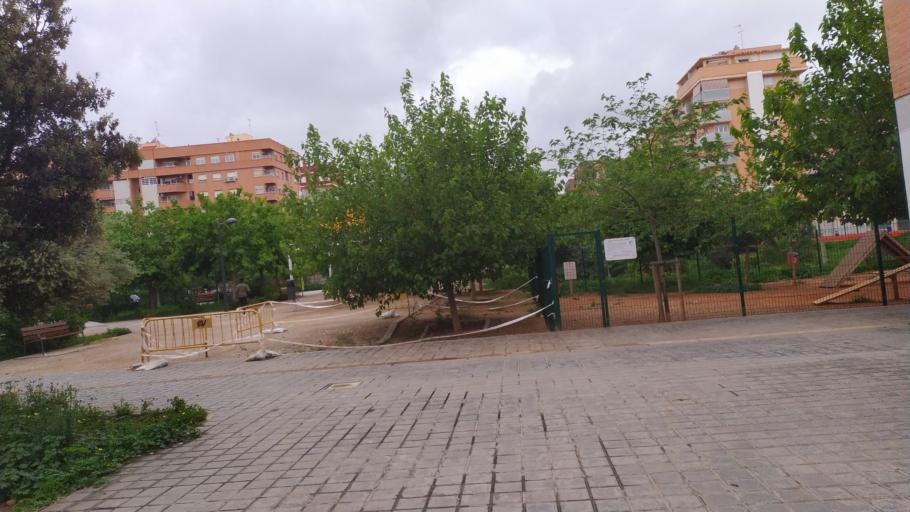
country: ES
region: Valencia
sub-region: Provincia de Valencia
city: Mislata
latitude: 39.4680
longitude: -0.4114
